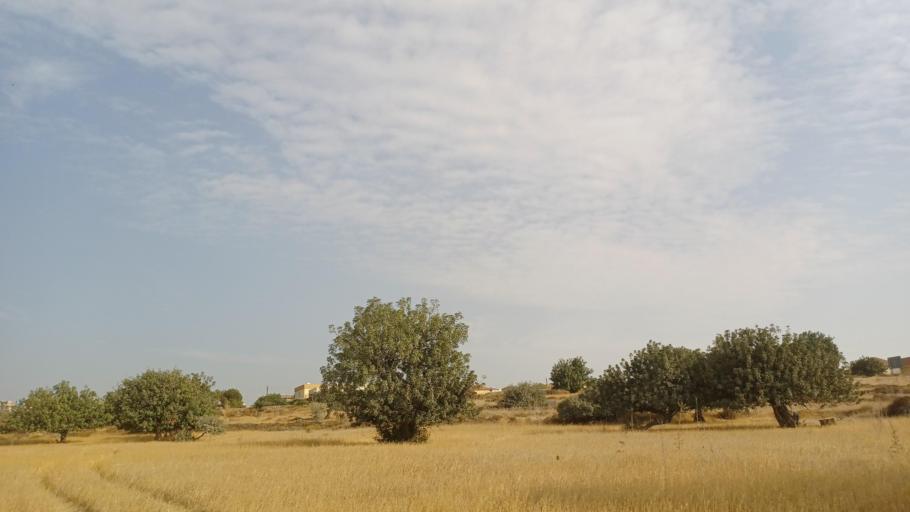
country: CY
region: Limassol
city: Ypsonas
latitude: 34.6937
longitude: 32.9417
